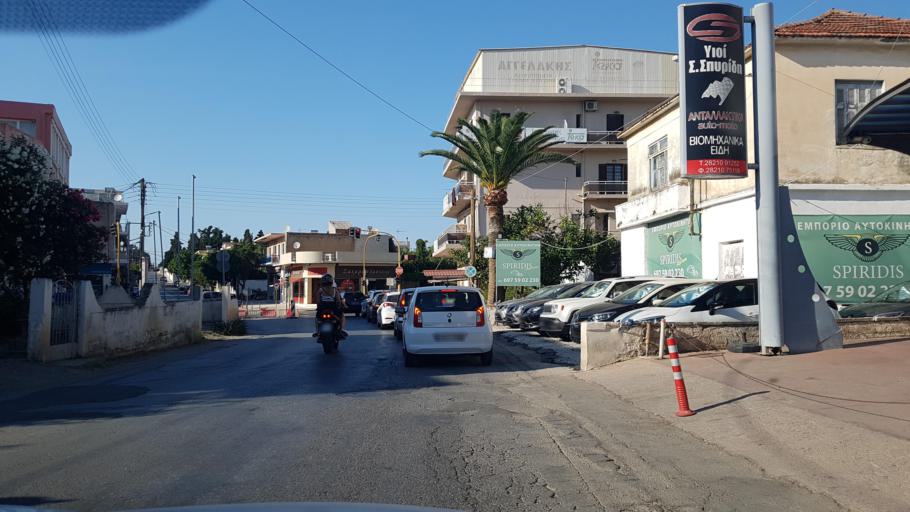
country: GR
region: Crete
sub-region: Nomos Chanias
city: Chania
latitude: 35.5036
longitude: 24.0196
